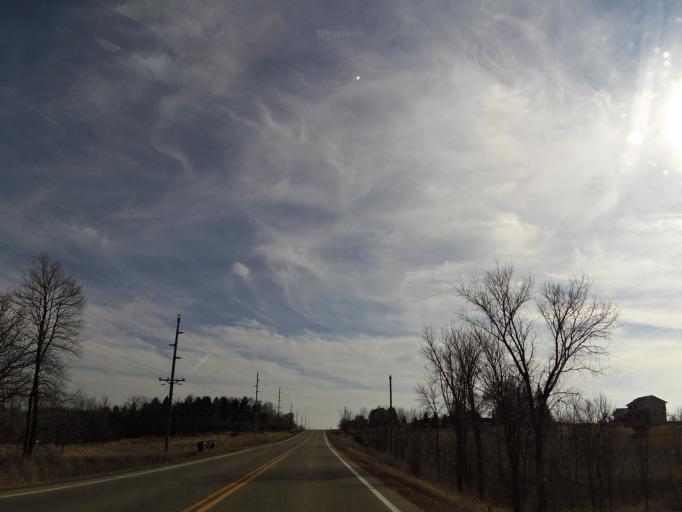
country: US
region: Minnesota
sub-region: Scott County
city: Prior Lake
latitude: 44.6239
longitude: -93.4403
